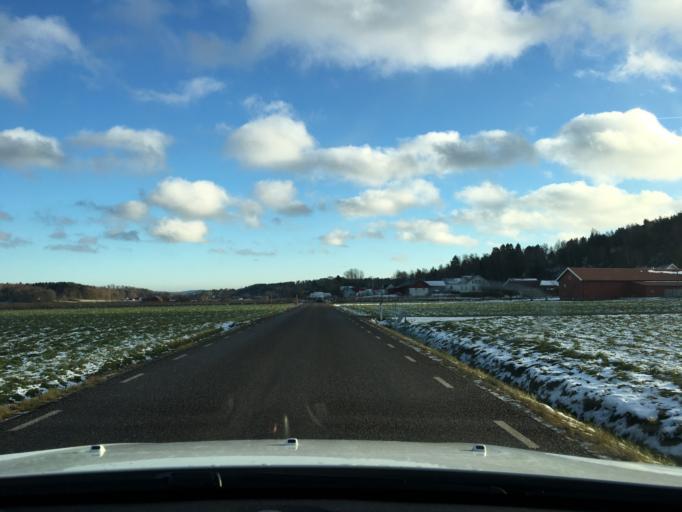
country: SE
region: Vaestra Goetaland
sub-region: Tjorns Kommun
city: Myggenas
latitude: 58.0484
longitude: 11.7188
